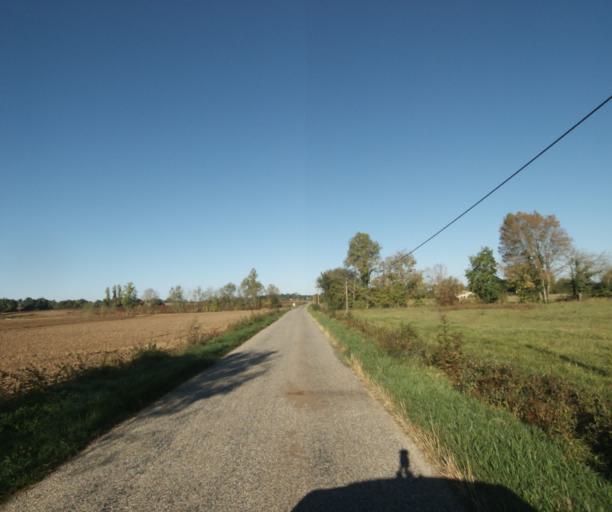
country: FR
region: Midi-Pyrenees
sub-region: Departement du Gers
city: Gondrin
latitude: 43.8478
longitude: 0.2380
